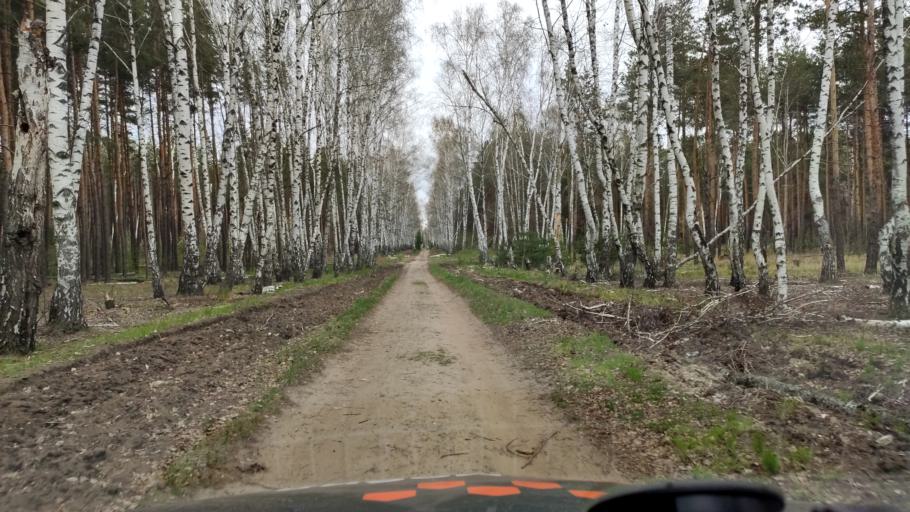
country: RU
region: Voronezj
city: Somovo
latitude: 51.7437
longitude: 39.2751
